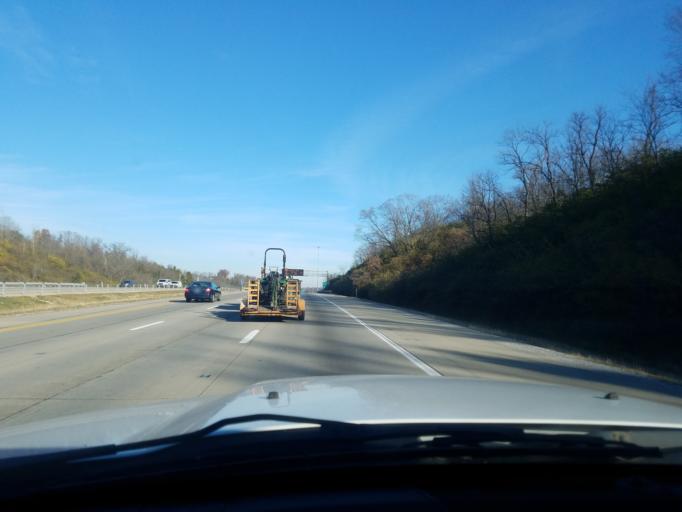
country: US
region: Kentucky
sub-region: Campbell County
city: Highland Heights
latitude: 39.0316
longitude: -84.4704
